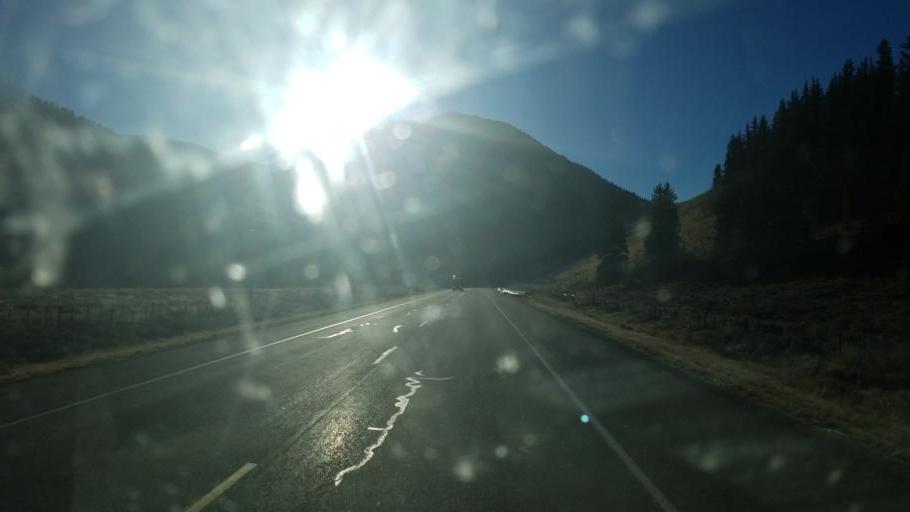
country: US
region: Colorado
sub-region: Gunnison County
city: Crested Butte
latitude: 38.7987
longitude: -106.8819
